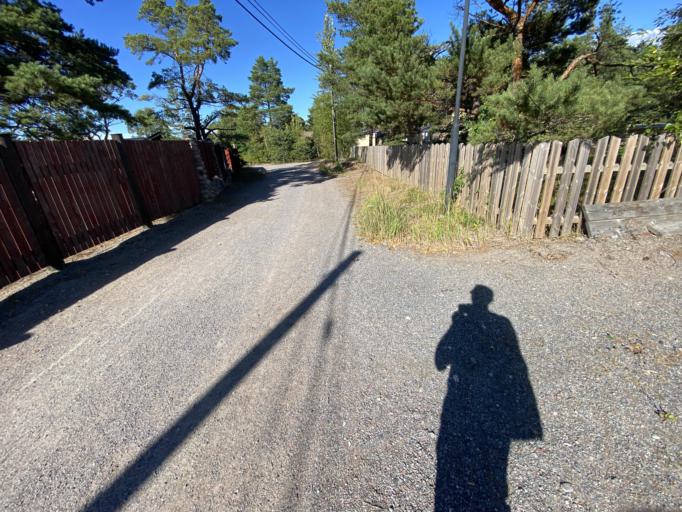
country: SE
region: Stockholm
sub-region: Varmdo Kommun
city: Holo
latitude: 59.2868
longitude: 18.9087
